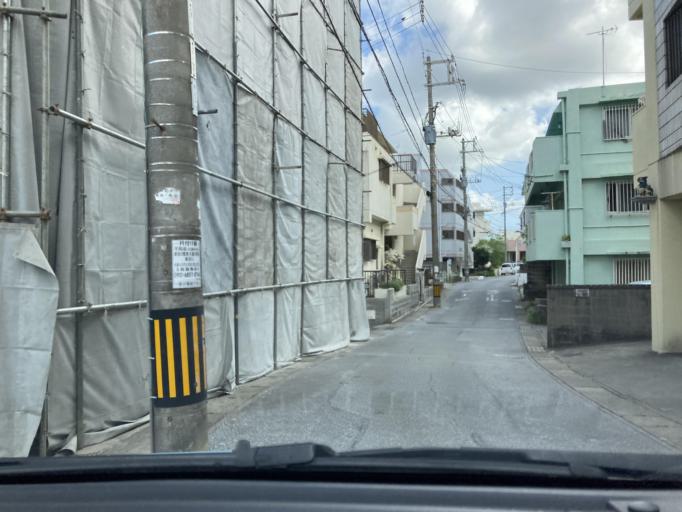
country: JP
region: Okinawa
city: Tomigusuku
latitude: 26.1979
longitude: 127.6747
